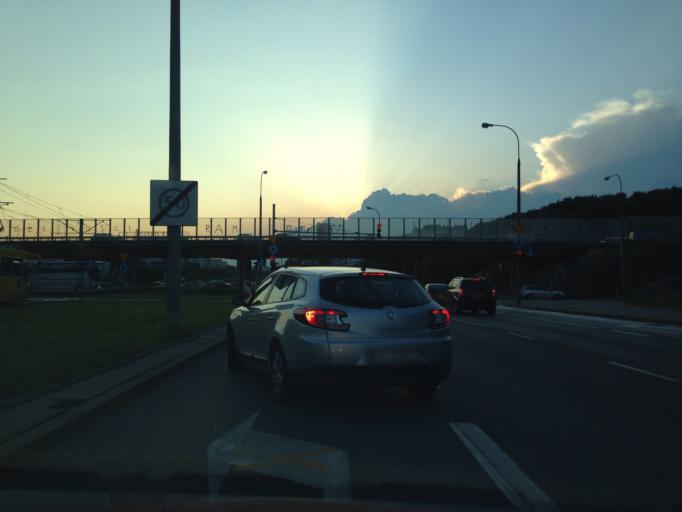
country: PL
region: Masovian Voivodeship
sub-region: Warszawa
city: Zoliborz
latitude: 52.2675
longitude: 20.9608
